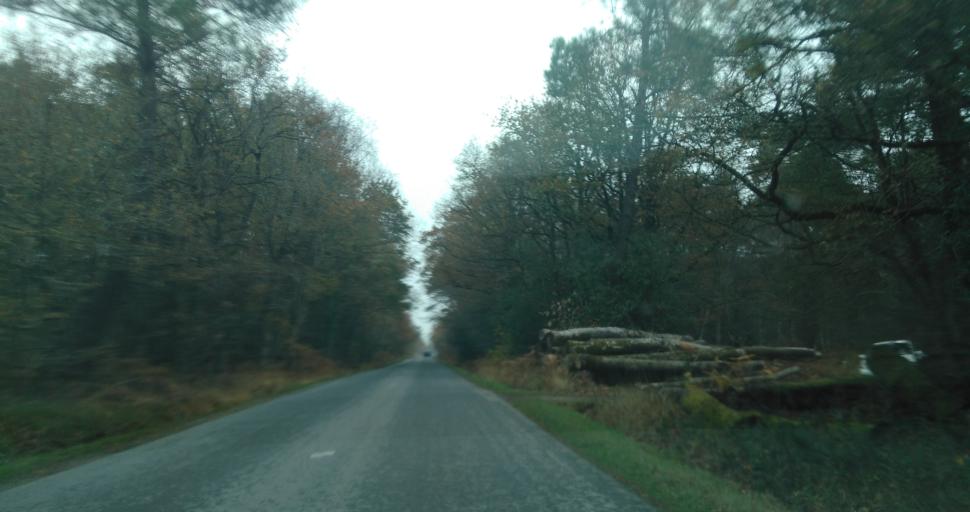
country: FR
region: Brittany
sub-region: Departement d'Ille-et-Vilaine
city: Iffendic
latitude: 48.0973
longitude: -2.0439
